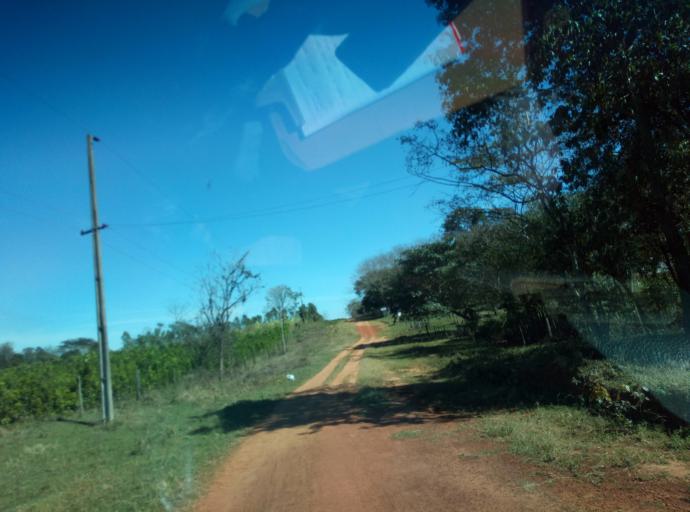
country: PY
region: Caaguazu
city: Doctor Cecilio Baez
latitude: -25.1789
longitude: -56.2441
